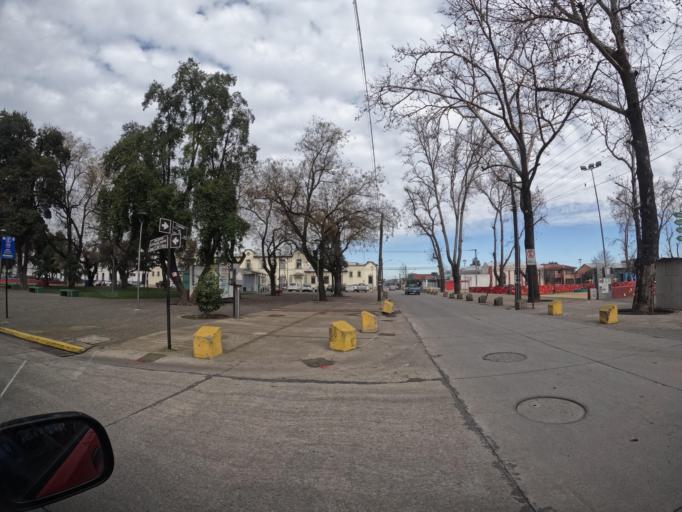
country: CL
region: Maule
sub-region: Provincia de Linares
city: Linares
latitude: -35.8483
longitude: -71.5999
